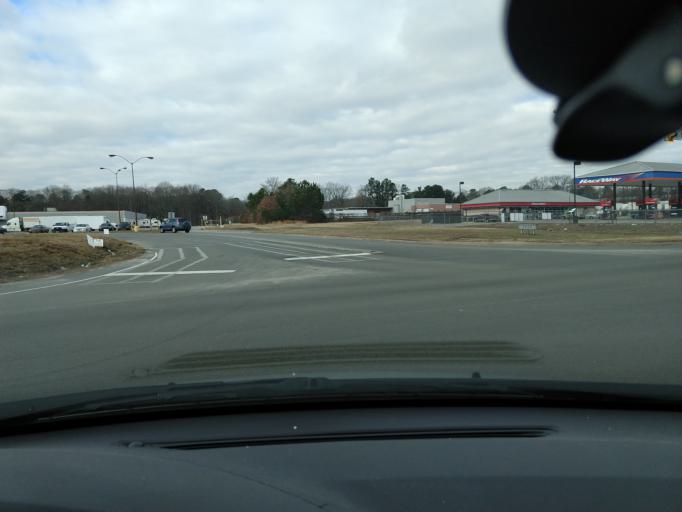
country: US
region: Virginia
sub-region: Chesterfield County
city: Bensley
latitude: 37.4465
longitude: -77.4407
